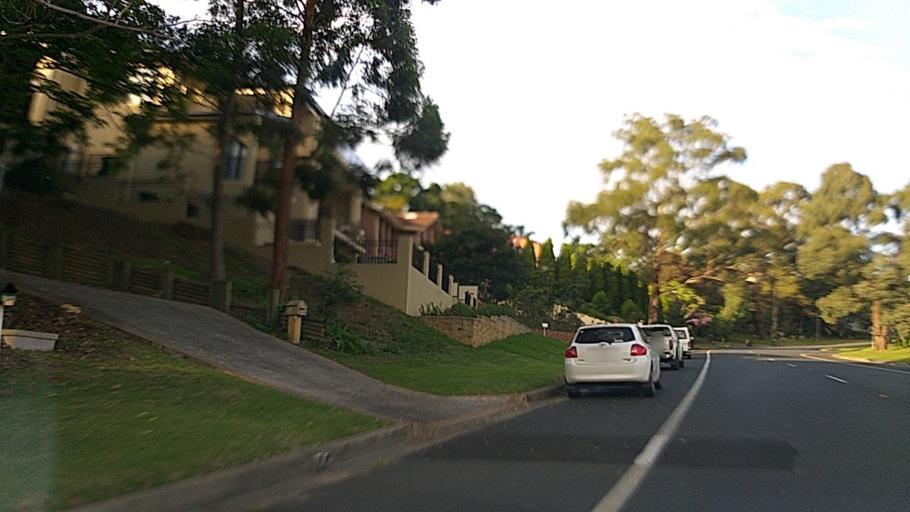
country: AU
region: New South Wales
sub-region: Wollongong
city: Mount Ousley
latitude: -34.3917
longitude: 150.8738
